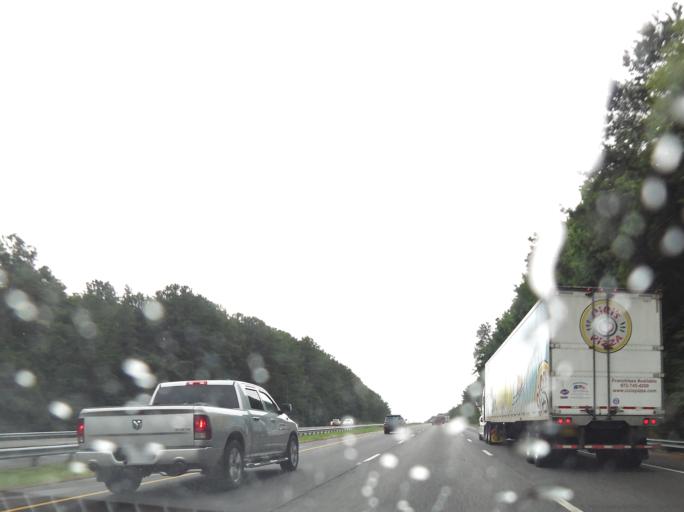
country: US
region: Georgia
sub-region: Houston County
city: Perry
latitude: 32.3892
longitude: -83.7673
